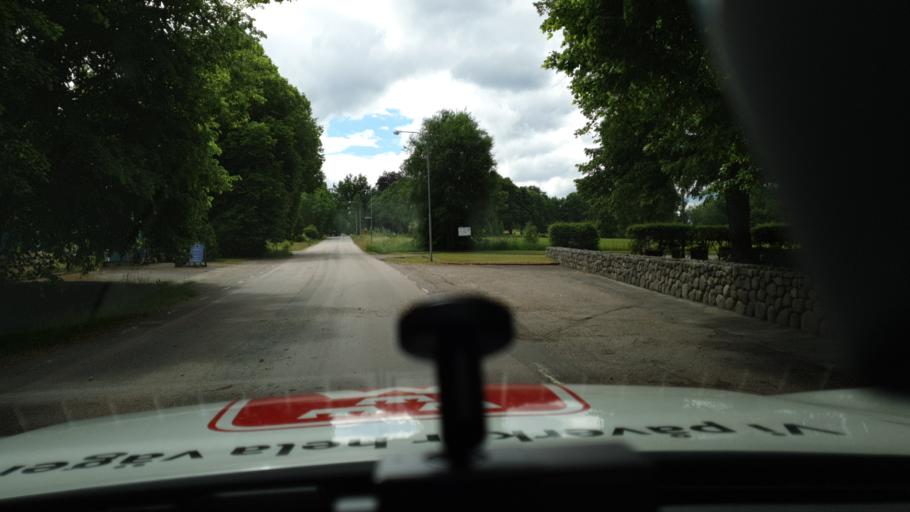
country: SE
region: Vaestra Goetaland
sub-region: Karlsborgs Kommun
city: Molltorp
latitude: 58.6581
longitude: 14.3997
